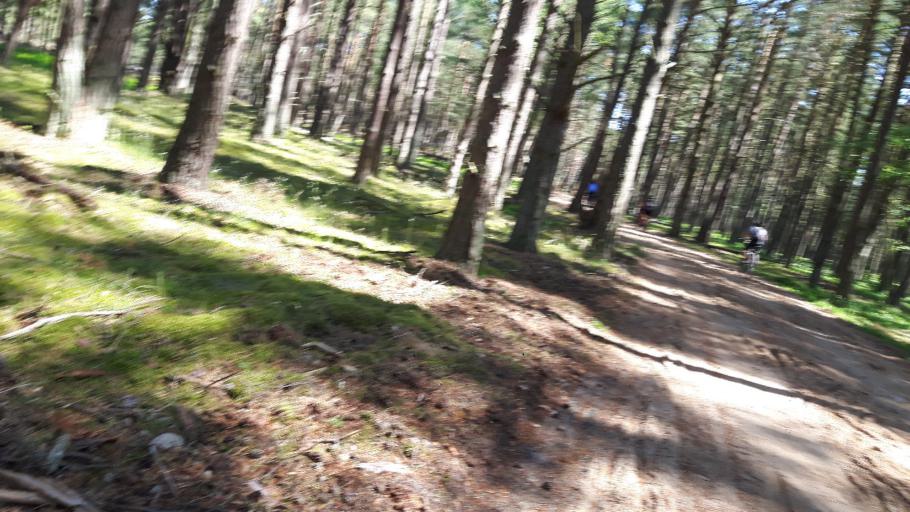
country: PL
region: Pomeranian Voivodeship
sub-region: Powiat slupski
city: Smoldzino
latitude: 54.6767
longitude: 17.1337
